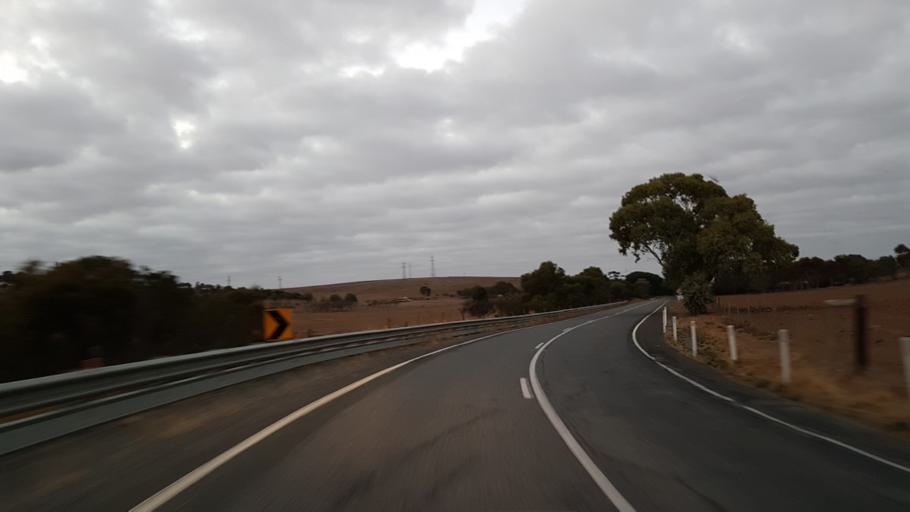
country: AU
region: South Australia
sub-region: Mount Barker
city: Callington
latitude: -35.0550
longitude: 139.0100
